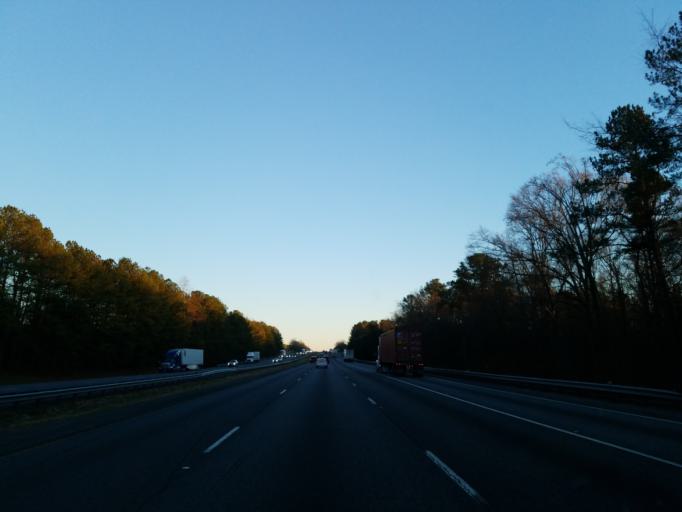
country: US
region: Georgia
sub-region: Monroe County
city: Forsyth
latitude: 33.0750
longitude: -83.9810
